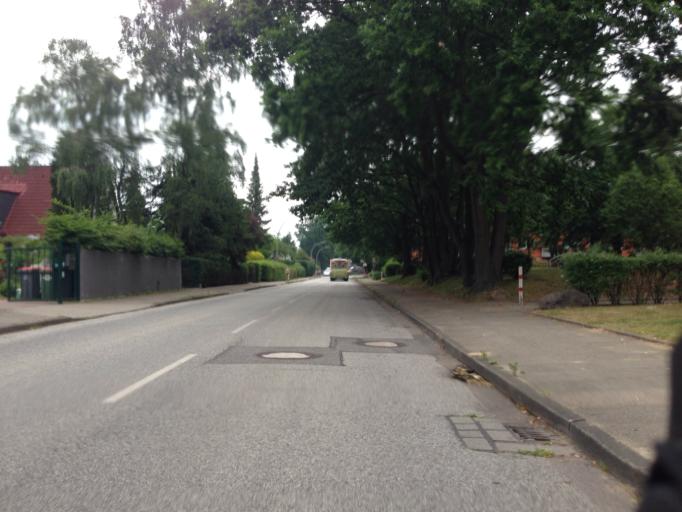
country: DE
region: Schleswig-Holstein
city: Barsbuettel
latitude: 53.5781
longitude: 10.1441
